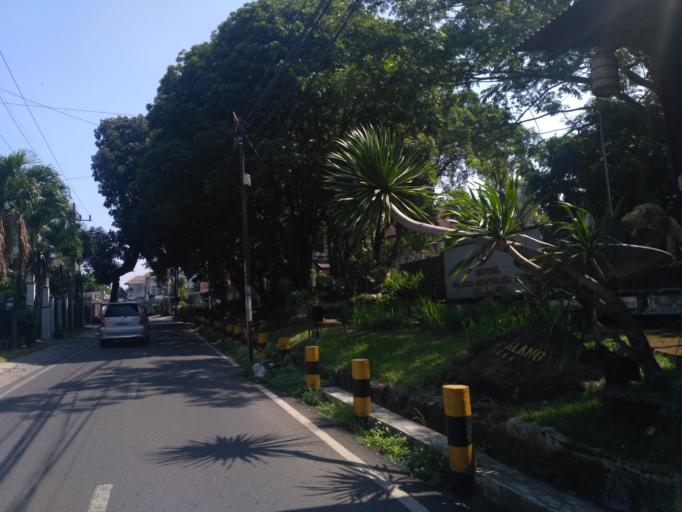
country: ID
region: East Java
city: Malang
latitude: -7.9388
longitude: 112.6239
